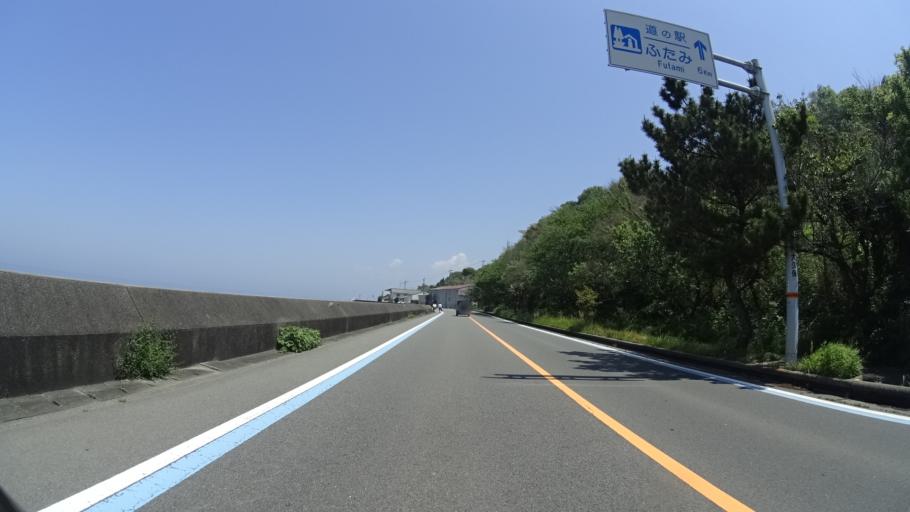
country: JP
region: Ehime
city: Iyo
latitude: 33.6559
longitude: 132.5896
